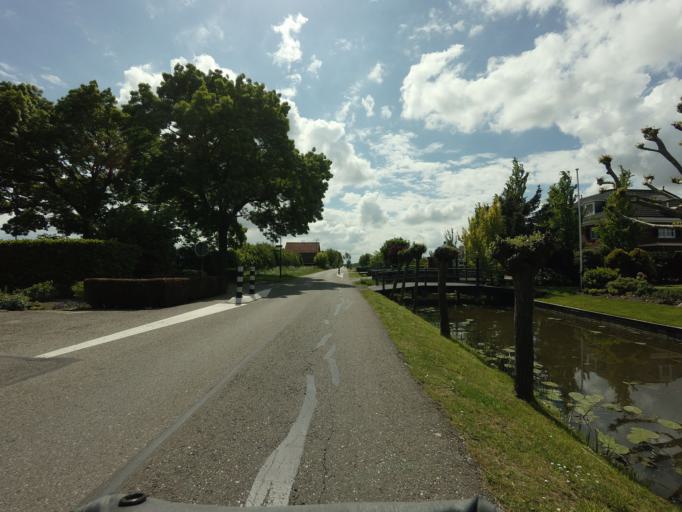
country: NL
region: South Holland
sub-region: Gemeente Gorinchem
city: Gorinchem
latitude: 51.8727
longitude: 4.9482
